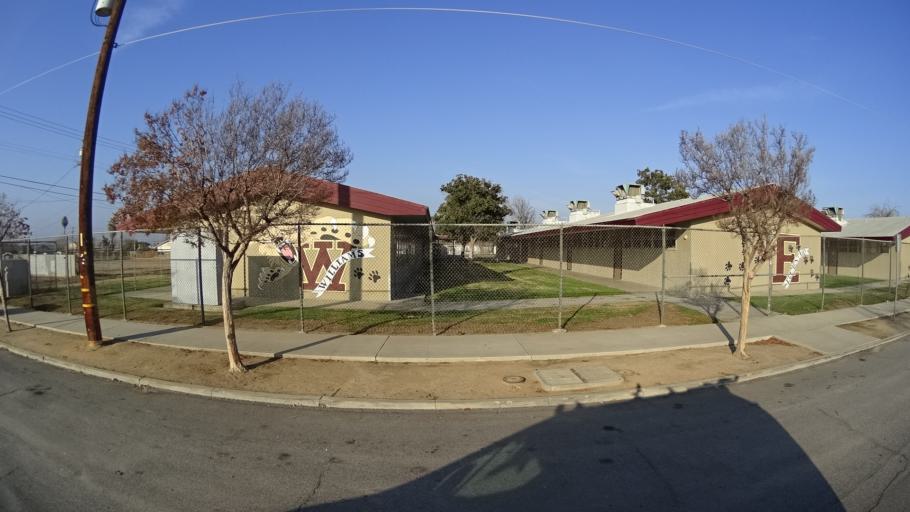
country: US
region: California
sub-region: Kern County
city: Bakersfield
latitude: 35.3775
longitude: -118.9758
